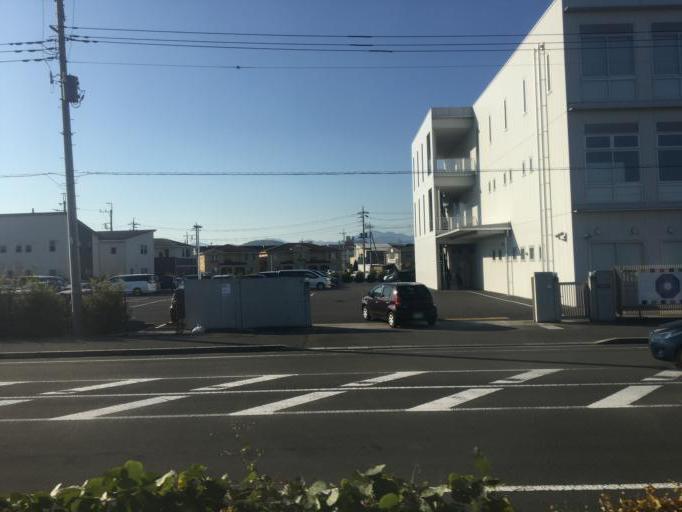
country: JP
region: Gunma
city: Takasaki
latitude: 36.3072
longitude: 139.0302
